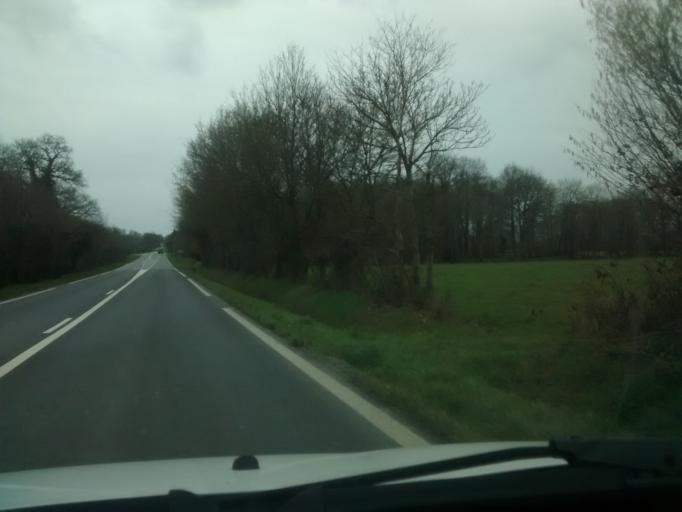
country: FR
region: Brittany
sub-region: Departement d'Ille-et-Vilaine
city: Sens-de-Bretagne
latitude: 48.3146
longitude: -1.5365
